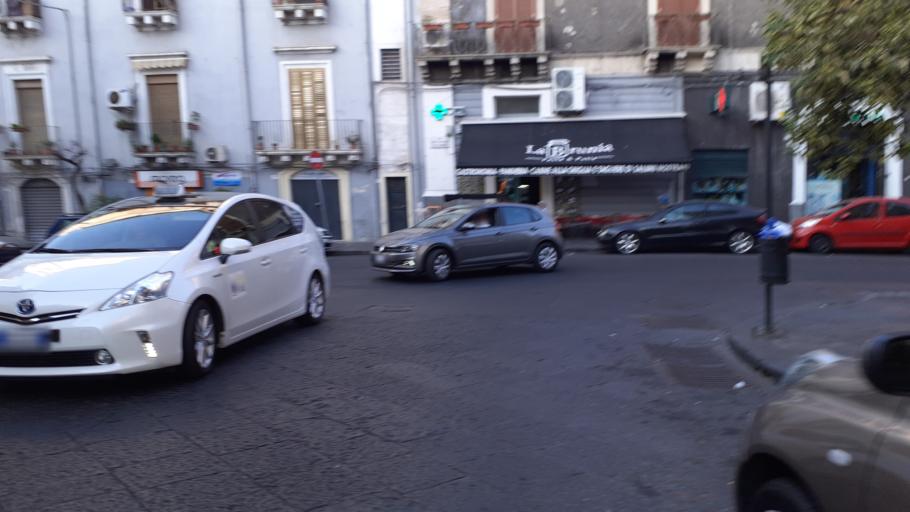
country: IT
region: Sicily
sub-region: Catania
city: Catania
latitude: 37.5003
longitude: 15.0876
